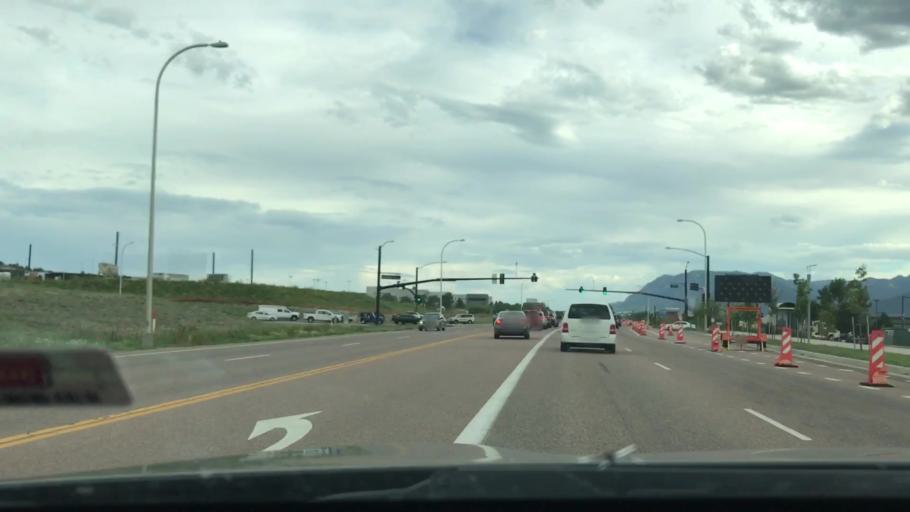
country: US
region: Colorado
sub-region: El Paso County
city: Colorado Springs
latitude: 38.9113
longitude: -104.8161
